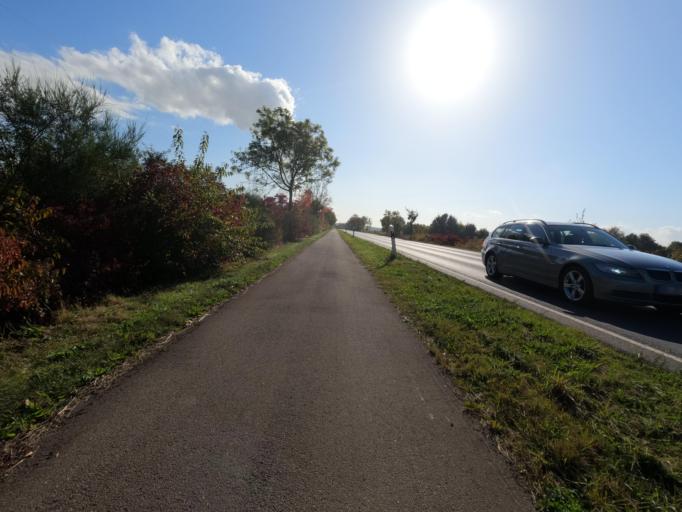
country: DE
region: North Rhine-Westphalia
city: Niedermerz
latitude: 50.8700
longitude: 6.2757
